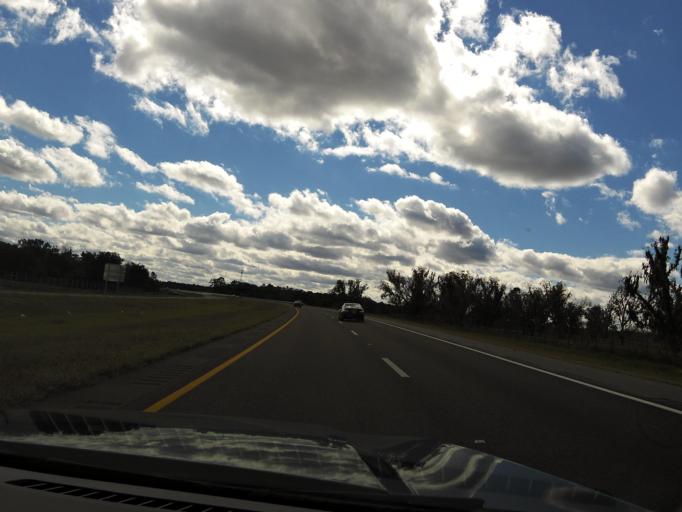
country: US
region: Florida
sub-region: Bradford County
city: Starke
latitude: 29.9280
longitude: -82.1382
